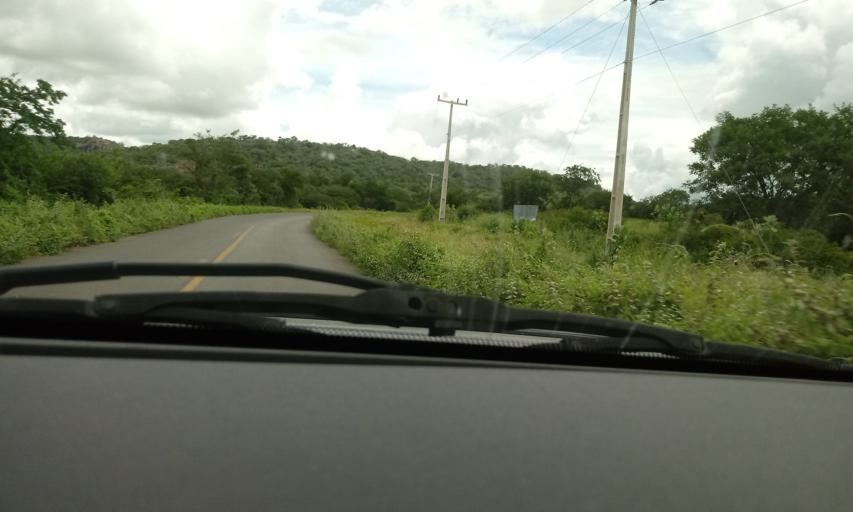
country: BR
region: Bahia
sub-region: Guanambi
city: Guanambi
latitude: -14.1464
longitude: -42.8396
